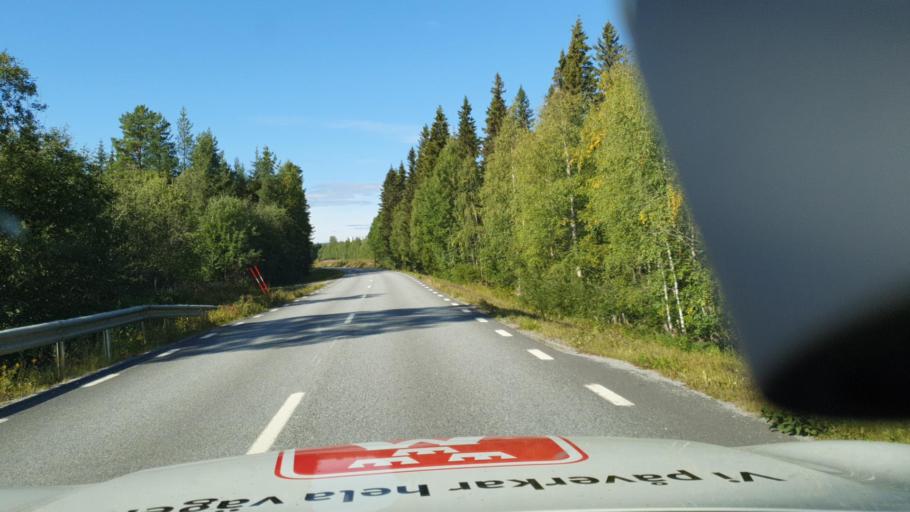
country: SE
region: Vaesterbotten
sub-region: Dorotea Kommun
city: Dorotea
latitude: 64.1088
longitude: 16.2363
